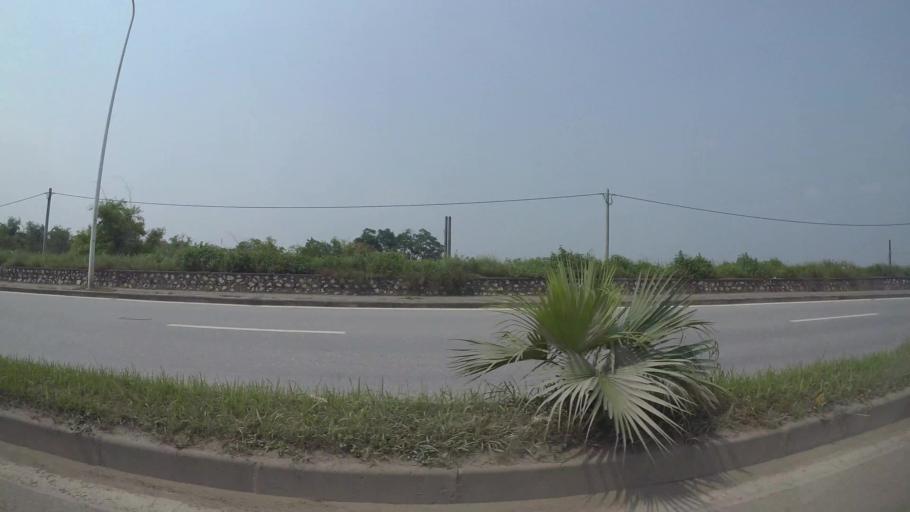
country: VN
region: Ha Noi
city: Tay Ho
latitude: 21.0897
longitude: 105.8009
